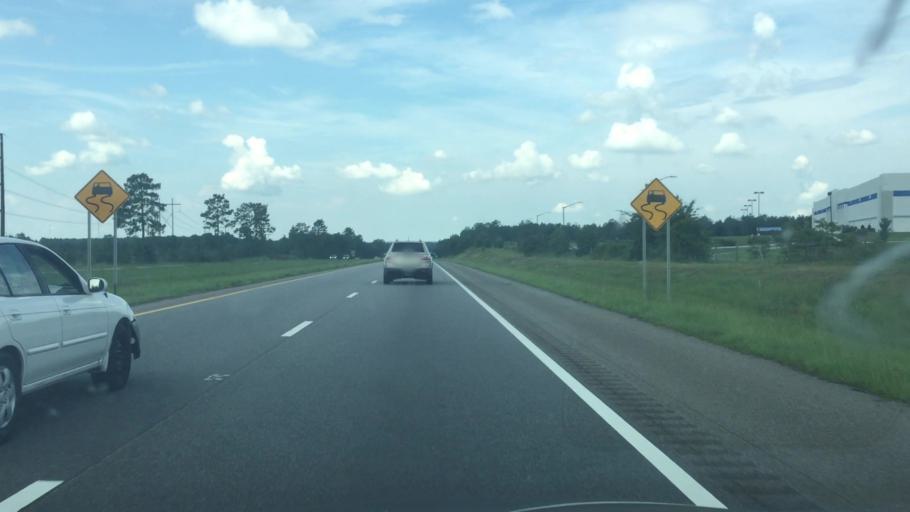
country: US
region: North Carolina
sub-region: Richmond County
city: Hamlet
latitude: 34.8543
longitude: -79.7116
